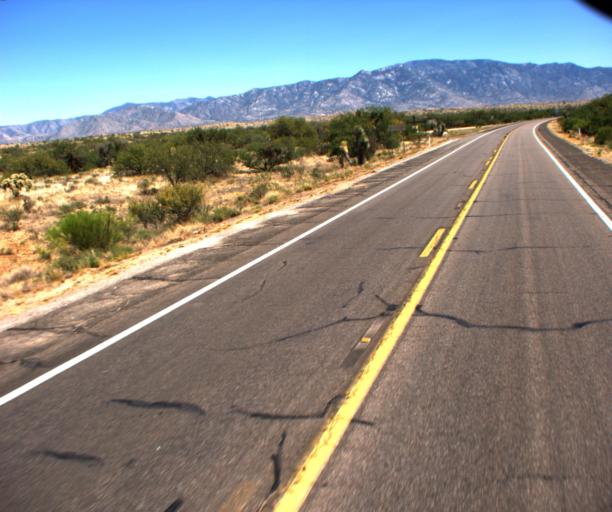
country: US
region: Arizona
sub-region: Pima County
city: Catalina
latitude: 32.5620
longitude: -110.9381
